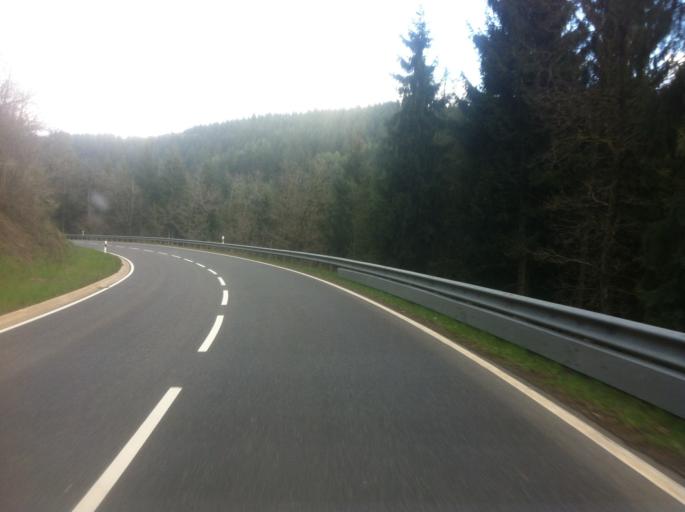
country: DE
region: Rheinland-Pfalz
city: Preischeid
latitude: 50.0491
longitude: 6.1575
